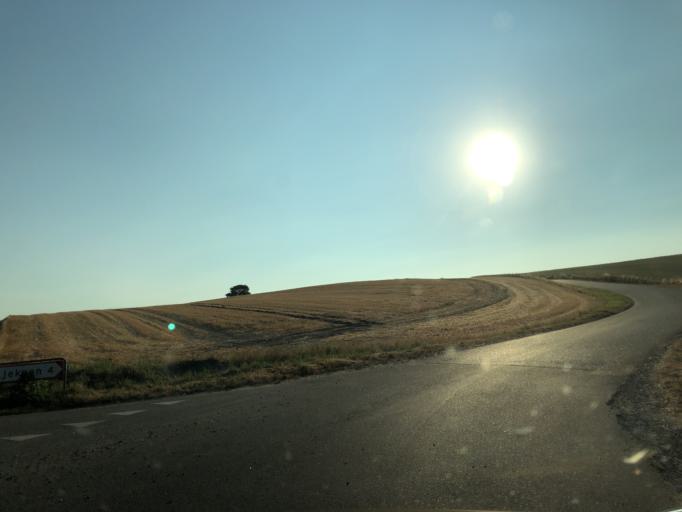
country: DK
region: Central Jutland
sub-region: Skanderborg Kommune
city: Skanderborg
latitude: 56.0880
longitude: 9.9096
